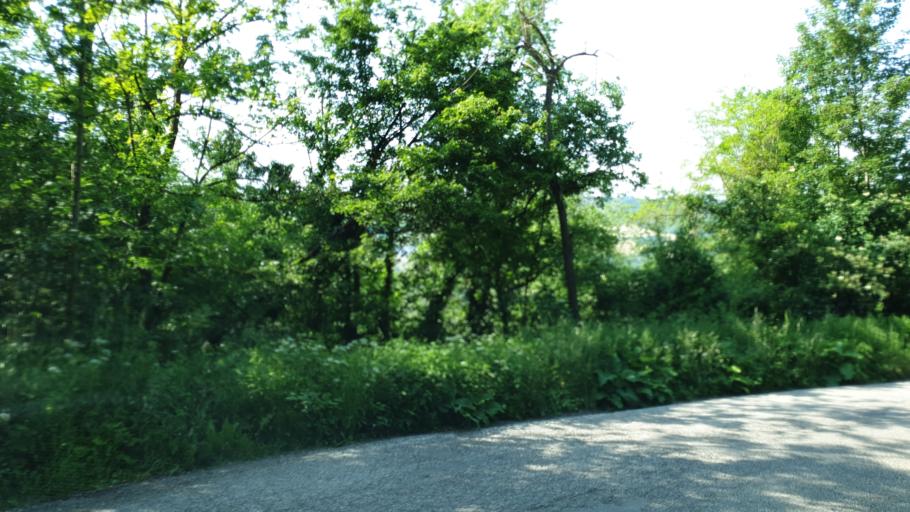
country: IT
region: Emilia-Romagna
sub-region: Forli-Cesena
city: Sarsina
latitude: 43.9128
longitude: 12.1701
